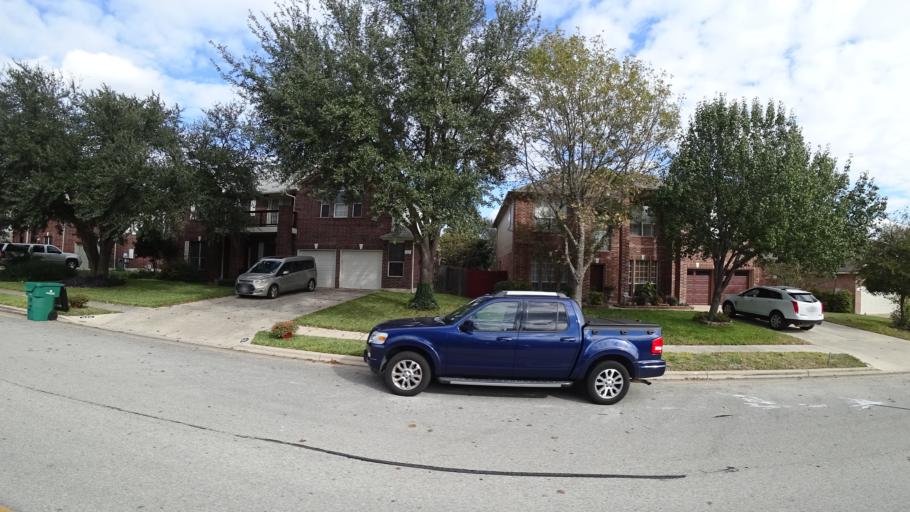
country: US
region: Texas
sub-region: Travis County
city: Pflugerville
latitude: 30.4297
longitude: -97.6292
